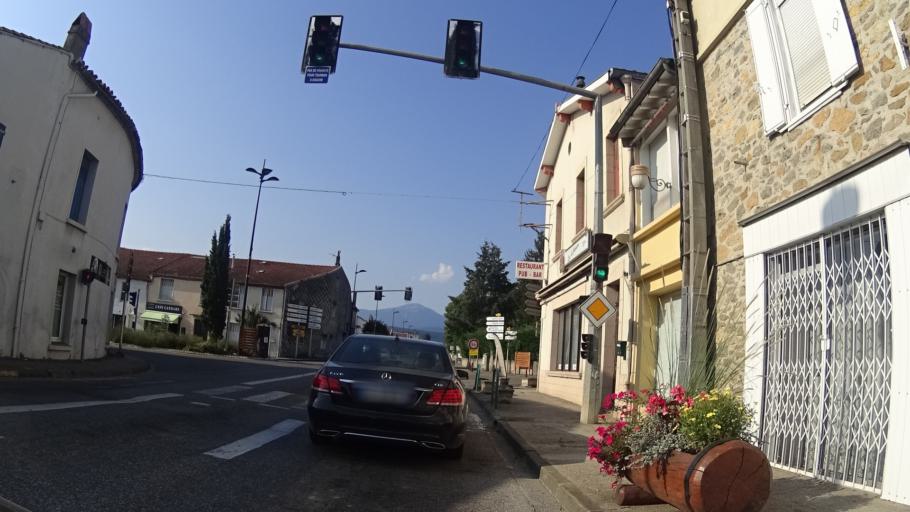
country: FR
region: Midi-Pyrenees
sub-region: Departement de l'Ariege
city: Lavelanet
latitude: 42.9716
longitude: 1.8667
